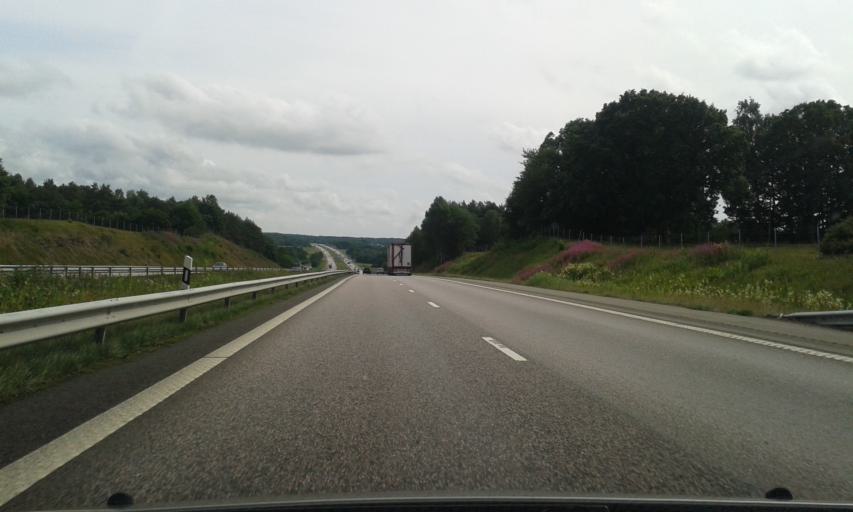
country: SE
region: Halland
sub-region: Kungsbacka Kommun
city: Frillesas
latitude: 57.2713
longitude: 12.2152
